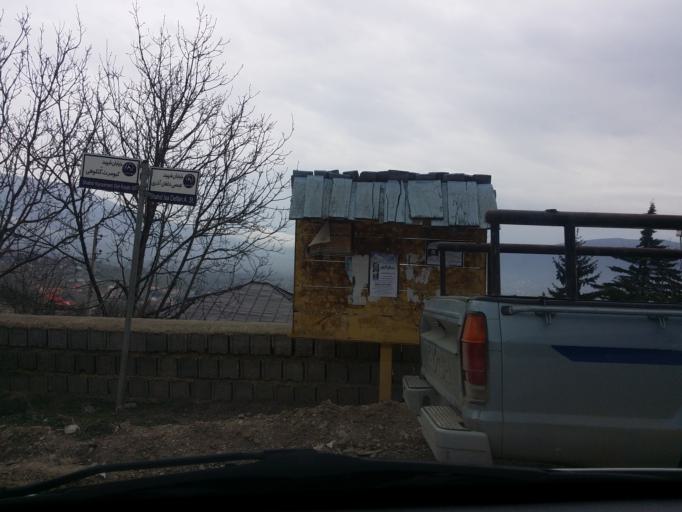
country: IR
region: Mazandaran
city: `Abbasabad
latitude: 36.5323
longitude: 51.1586
